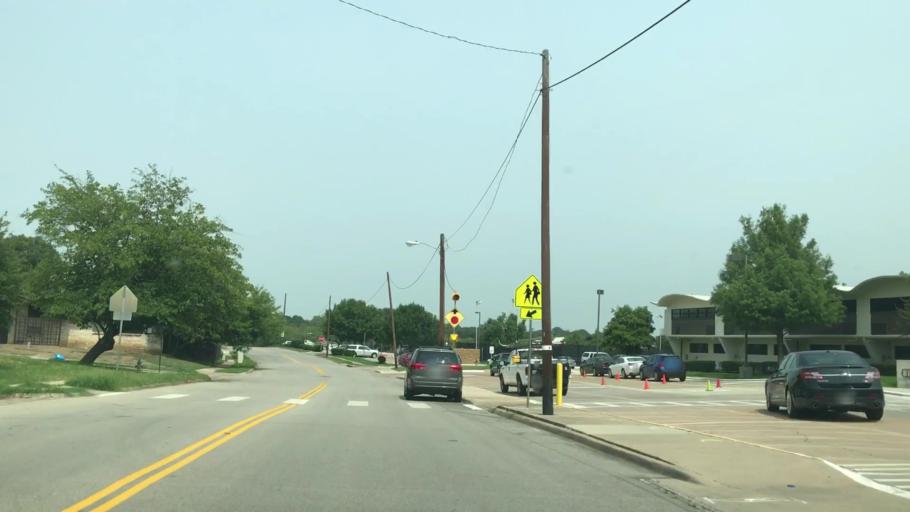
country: US
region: Texas
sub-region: Dallas County
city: Irving
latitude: 32.8432
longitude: -97.0041
